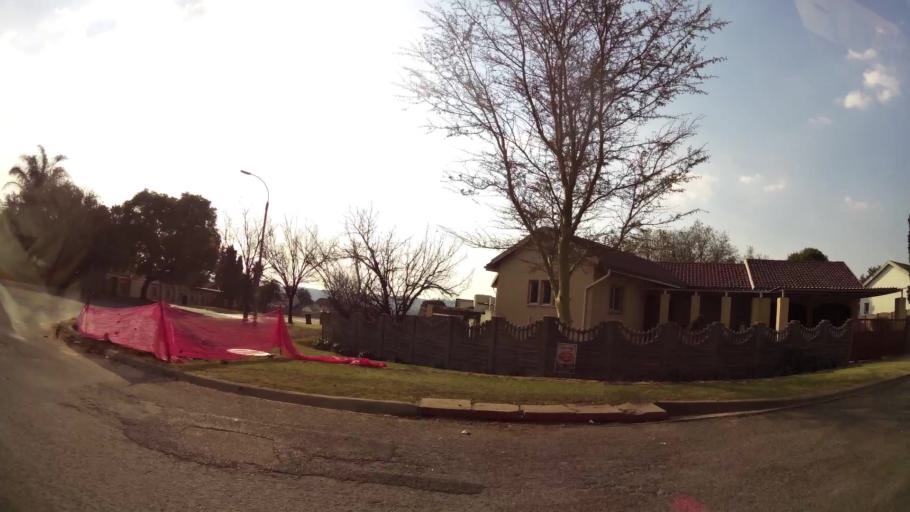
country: ZA
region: Gauteng
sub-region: City of Johannesburg Metropolitan Municipality
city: Modderfontein
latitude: -26.1051
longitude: 28.1883
